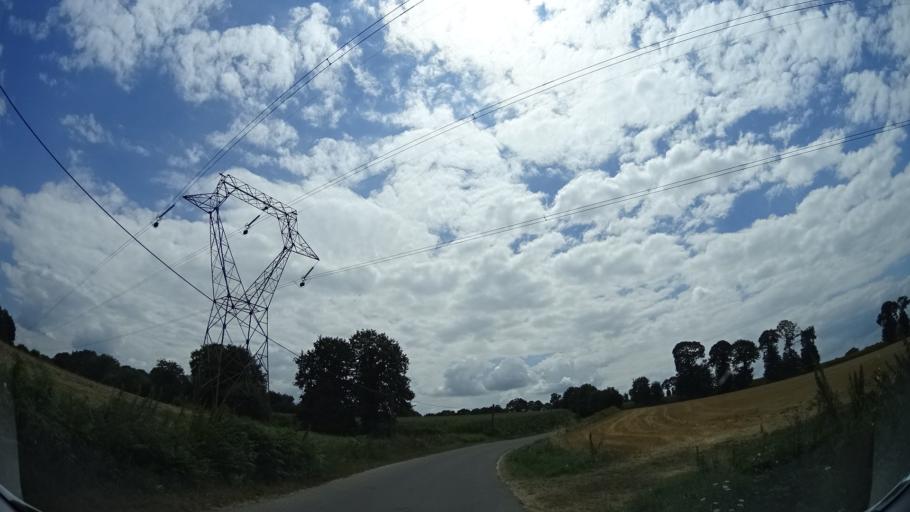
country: FR
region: Brittany
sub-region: Departement d'Ille-et-Vilaine
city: La Meziere
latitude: 48.1927
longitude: -1.7672
